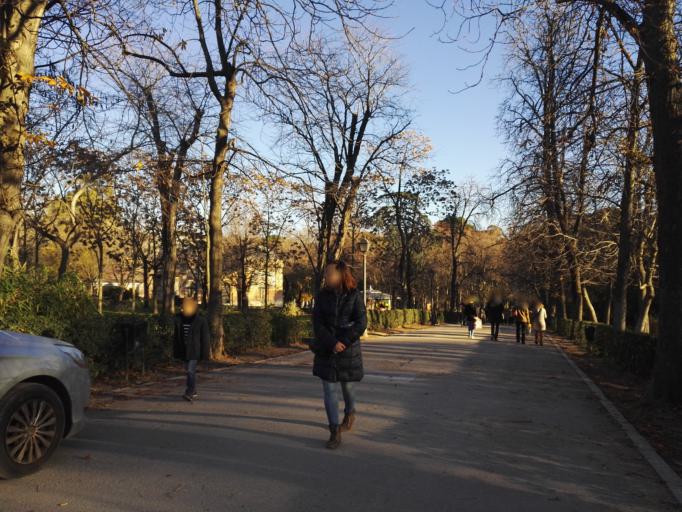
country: ES
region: Madrid
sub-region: Provincia de Madrid
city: Retiro
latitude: 40.4153
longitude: -3.6838
